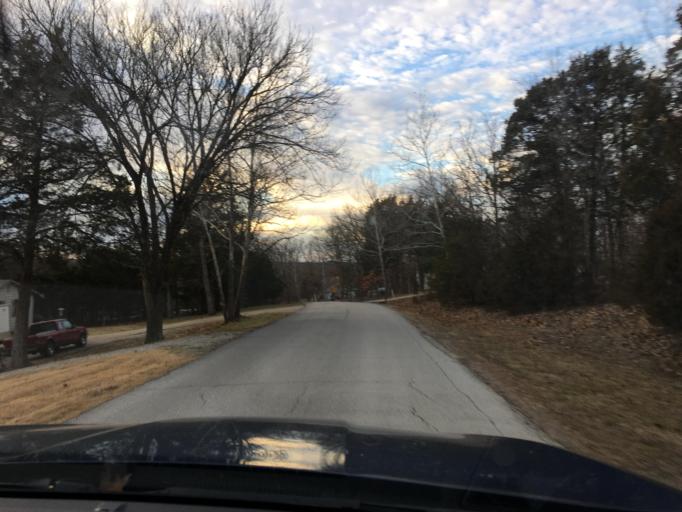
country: US
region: Missouri
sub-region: Jefferson County
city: De Soto
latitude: 38.0949
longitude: -90.5667
